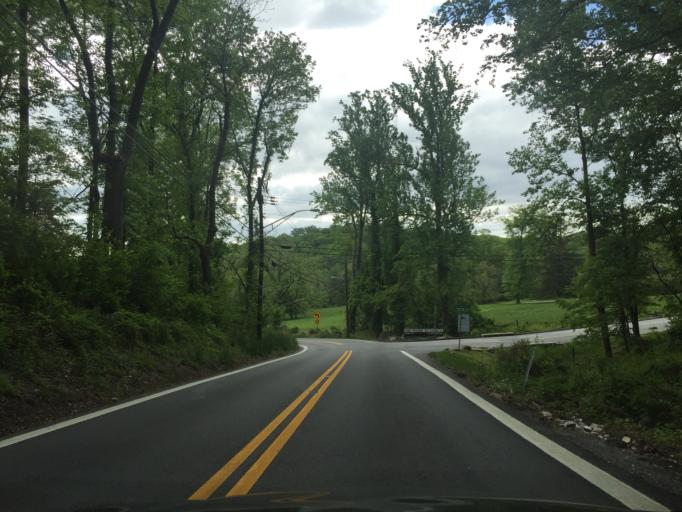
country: US
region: Maryland
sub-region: Baltimore County
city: Mays Chapel
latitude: 39.3967
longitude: -76.6739
